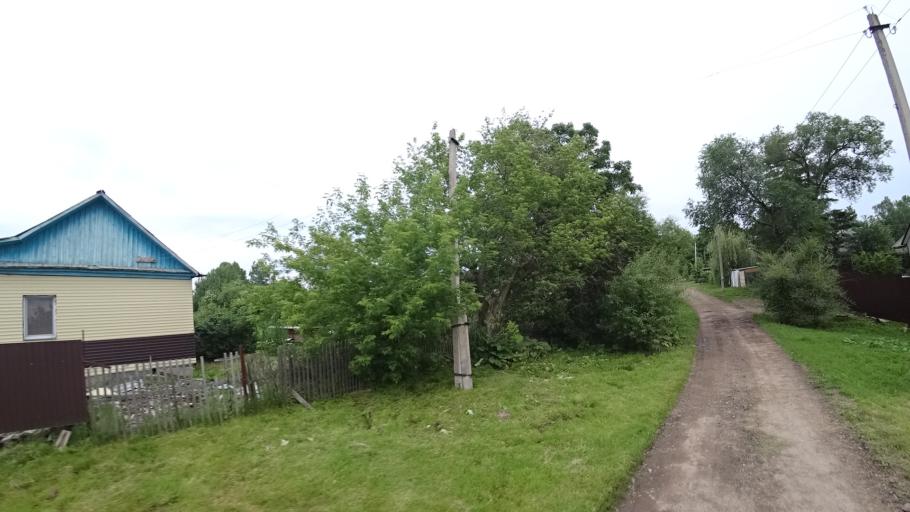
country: RU
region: Primorskiy
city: Novosysoyevka
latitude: 44.2234
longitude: 133.3539
